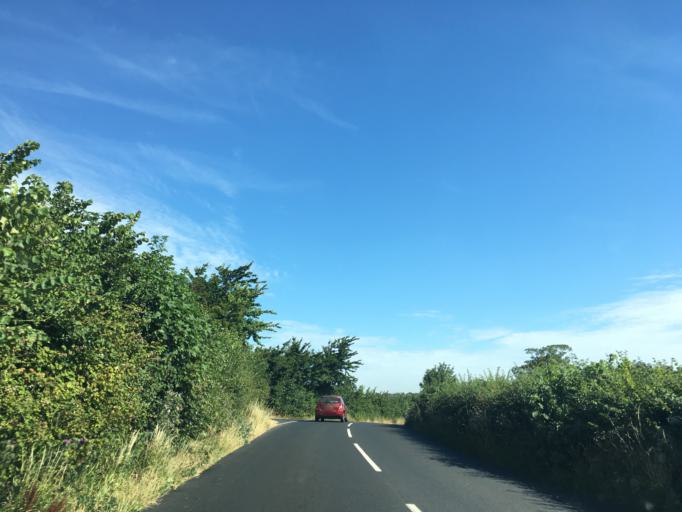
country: GB
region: England
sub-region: Isle of Wight
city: Newport
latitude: 50.6691
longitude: -1.3026
